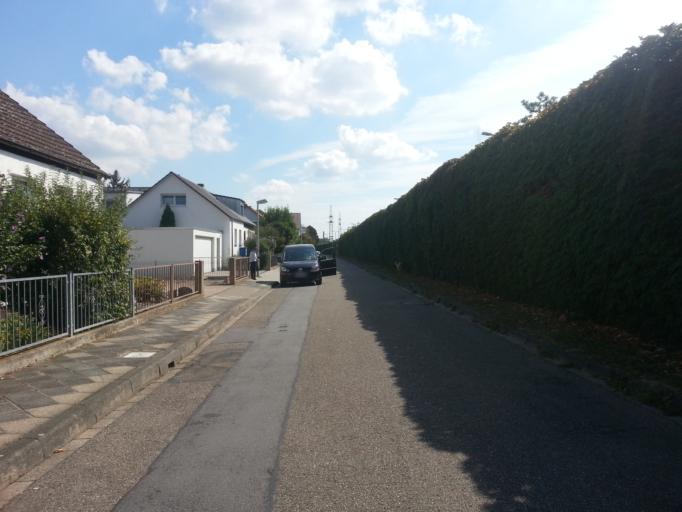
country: DE
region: Baden-Wuerttemberg
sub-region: Karlsruhe Region
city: Mannheim
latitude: 49.5216
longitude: 8.5058
